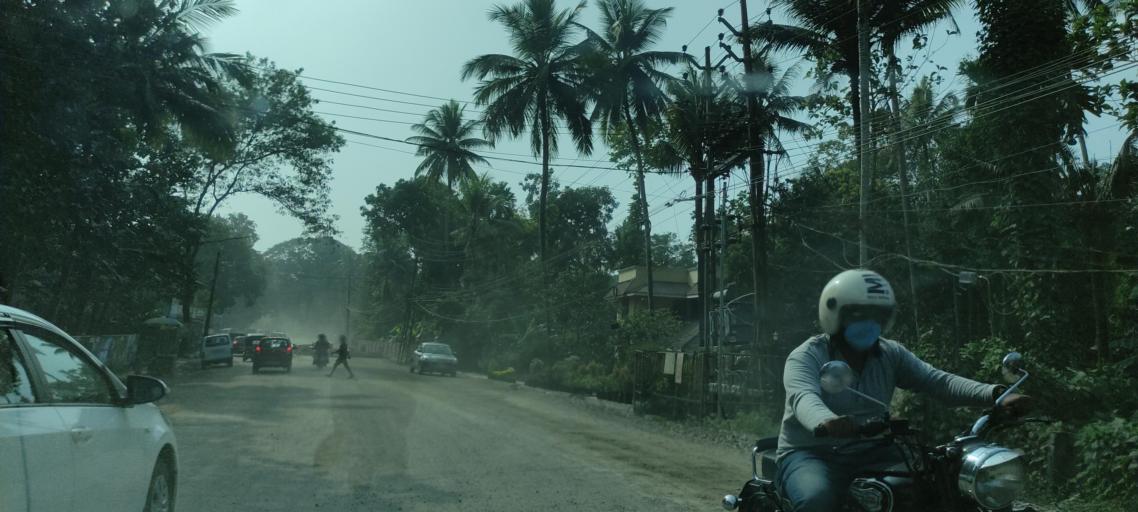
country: IN
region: Kerala
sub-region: Pattanamtitta
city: Tiruvalla
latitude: 9.3728
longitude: 76.5516
